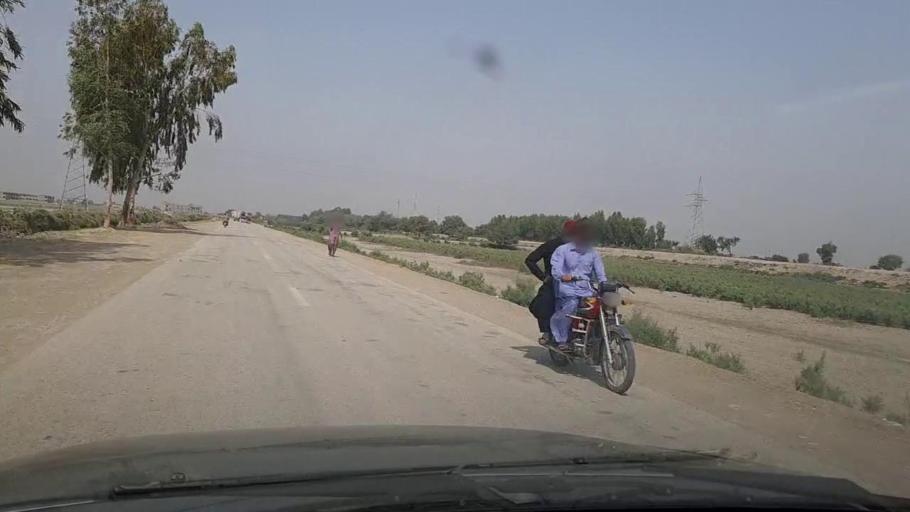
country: PK
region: Sindh
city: Thul
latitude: 28.3227
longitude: 68.7469
